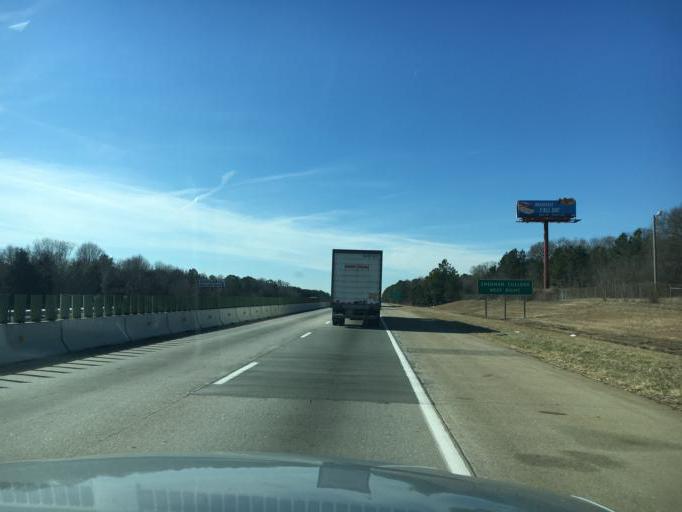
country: US
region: South Carolina
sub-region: Spartanburg County
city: Valley Falls
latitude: 35.0055
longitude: -81.9842
